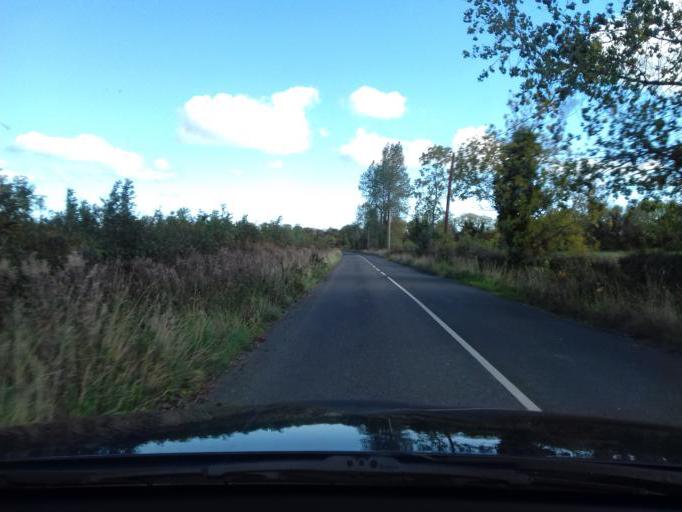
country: IE
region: Leinster
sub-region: An Mhi
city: Slane
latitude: 53.6875
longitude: -6.5108
